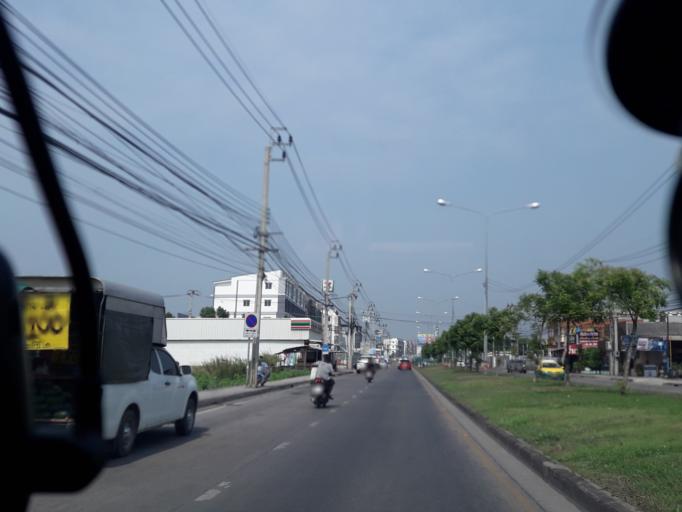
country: TH
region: Bangkok
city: Khlong Sam Wa
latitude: 13.8327
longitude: 100.7200
